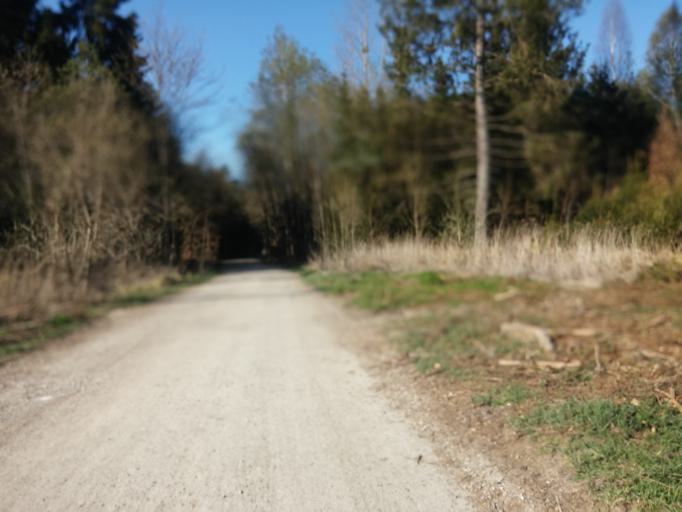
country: DE
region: Bavaria
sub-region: Upper Bavaria
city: Neubiberg
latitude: 48.0925
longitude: 11.6769
